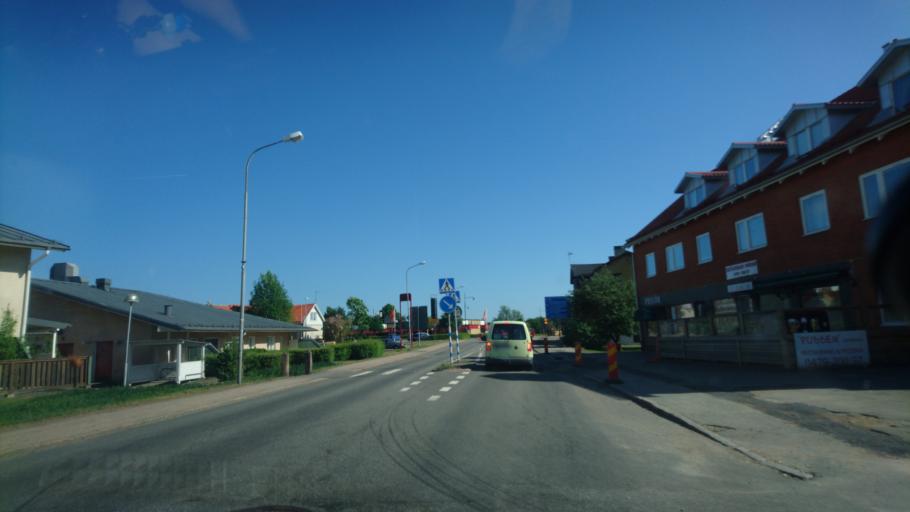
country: SE
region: Skane
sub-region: Osby Kommun
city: Lonsboda
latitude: 56.3986
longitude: 14.3195
